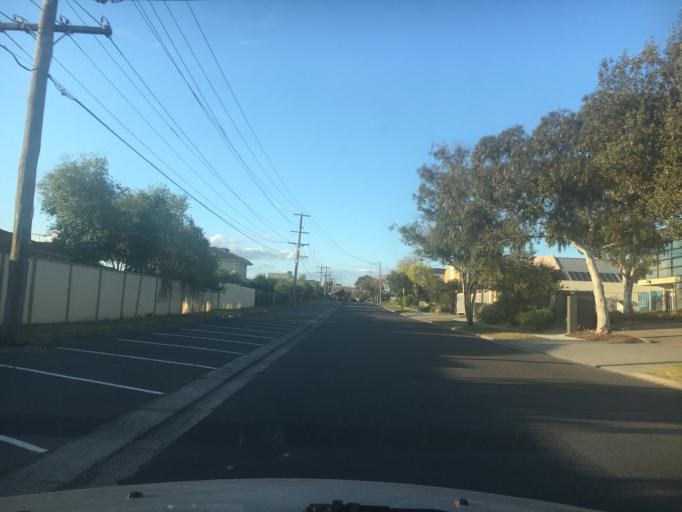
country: AU
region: Victoria
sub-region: Monash
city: Clayton
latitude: -37.9265
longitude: 145.1326
